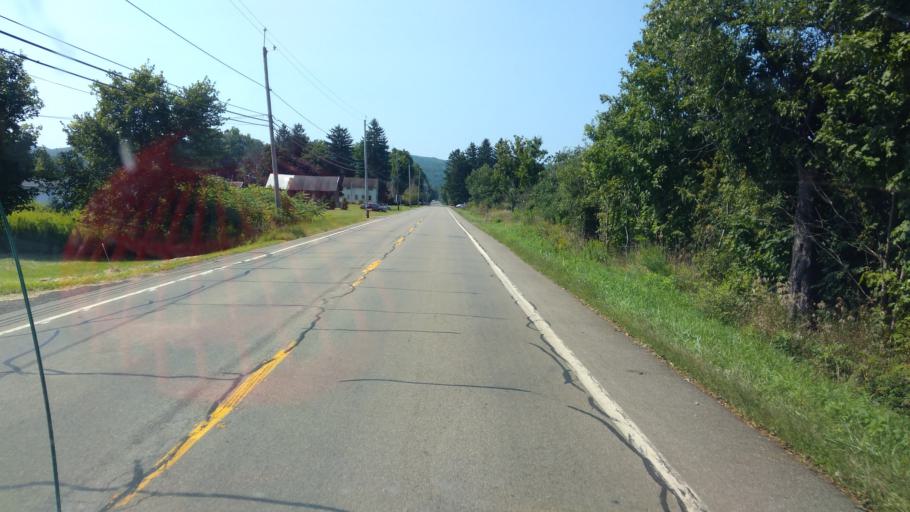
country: US
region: New York
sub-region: Allegany County
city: Belmont
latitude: 42.2343
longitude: -78.0246
